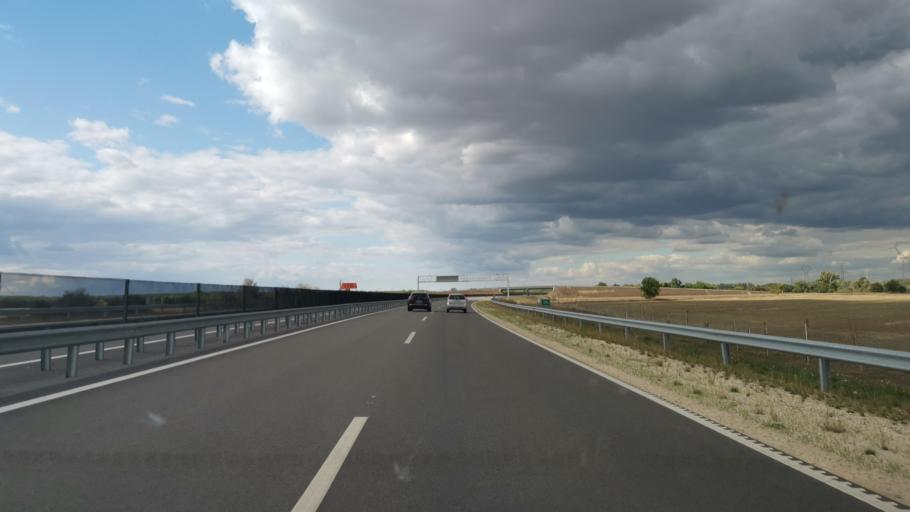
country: HU
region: Jasz-Nagykun-Szolnok
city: Tiszapuspoki
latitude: 47.1902
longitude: 20.3398
